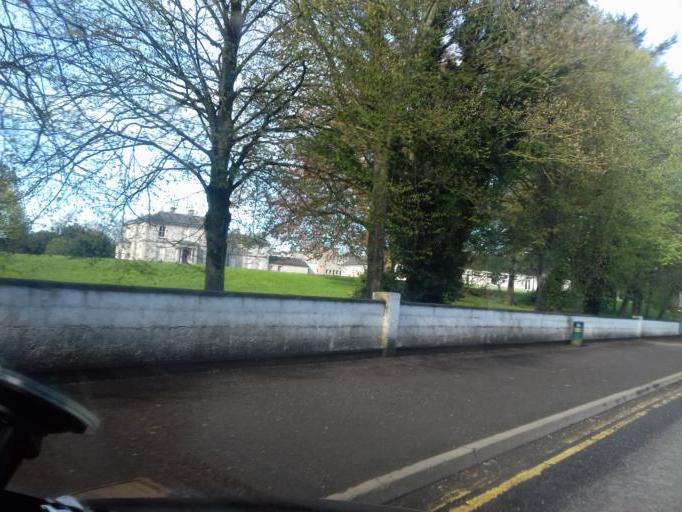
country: IE
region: Leinster
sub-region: An Mhi
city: Kells
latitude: 53.7260
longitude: -6.8701
